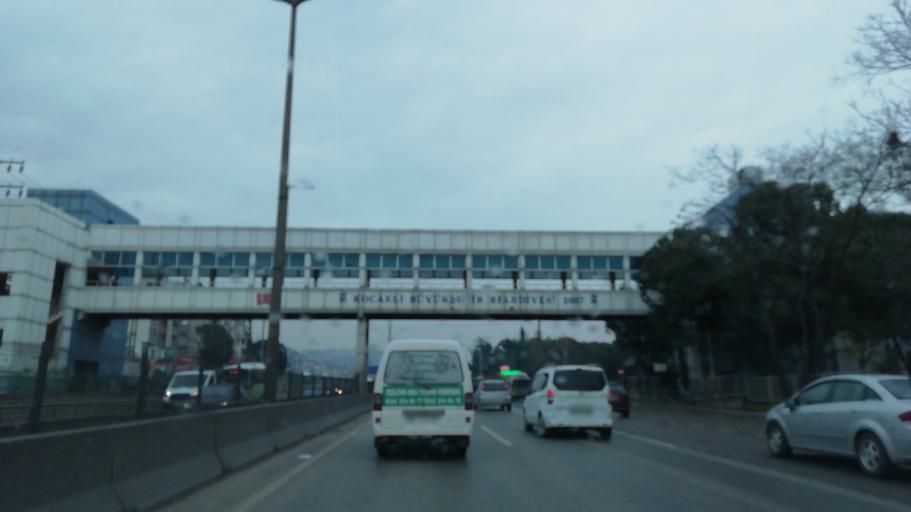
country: TR
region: Kocaeli
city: Izmit
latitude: 40.7645
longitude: 29.8950
